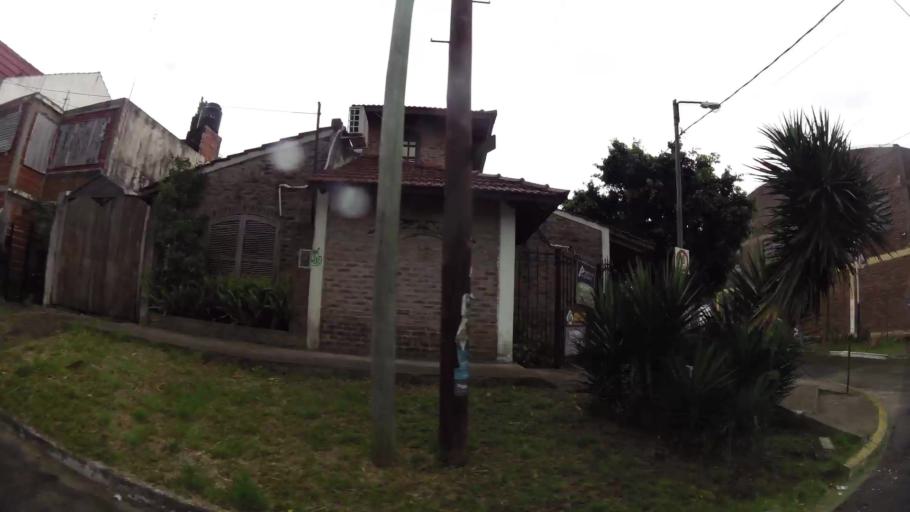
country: AR
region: Buenos Aires
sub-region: Partido de Quilmes
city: Quilmes
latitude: -34.7725
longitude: -58.2194
